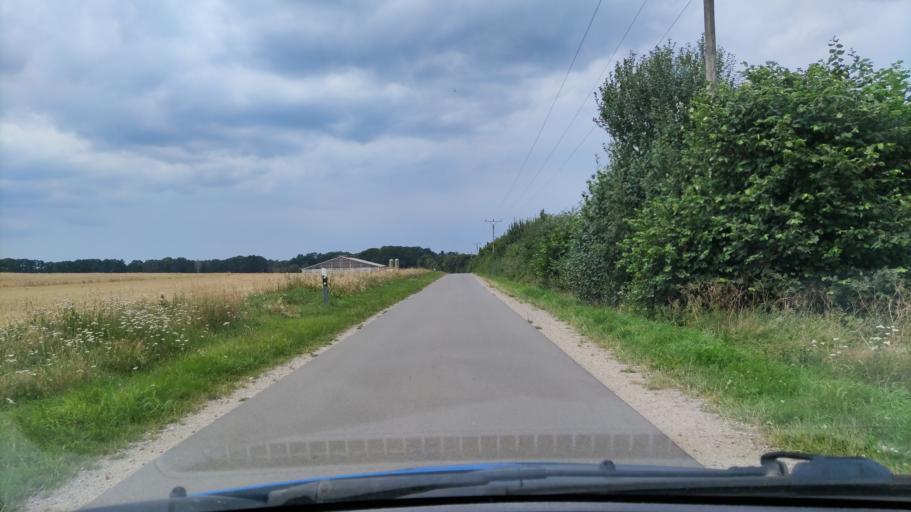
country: DE
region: Lower Saxony
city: Suhlendorf
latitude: 52.9506
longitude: 10.8386
